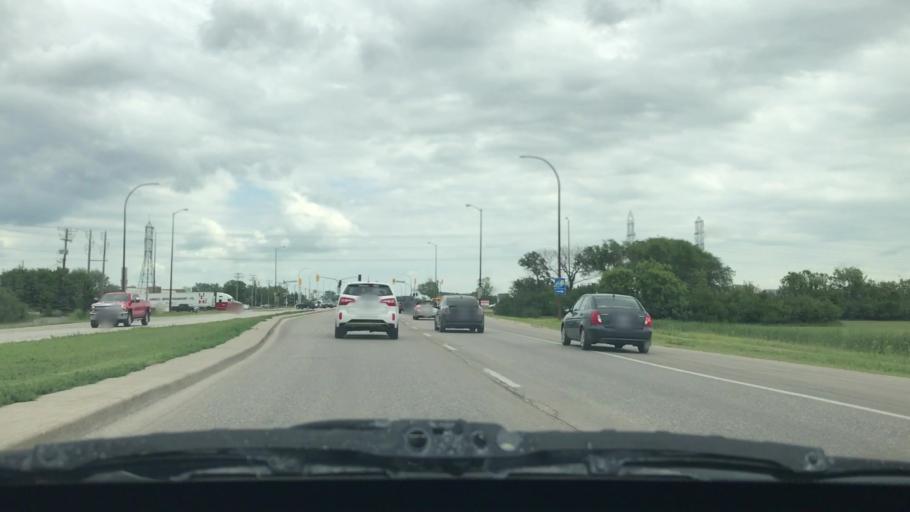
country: CA
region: Manitoba
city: Winnipeg
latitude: 49.8559
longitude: -97.0523
